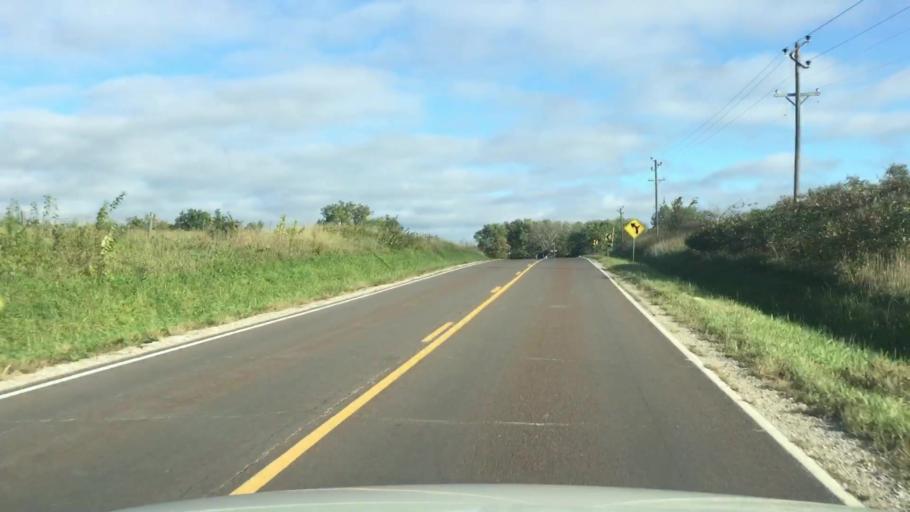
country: US
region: Missouri
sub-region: Howard County
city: New Franklin
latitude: 39.0588
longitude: -92.7441
